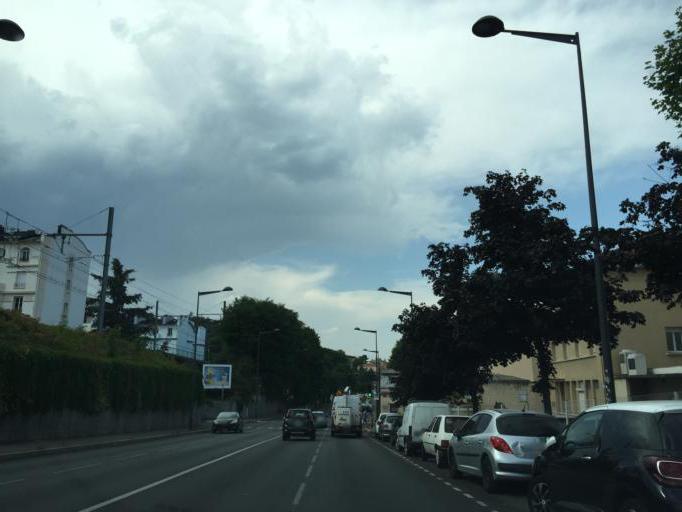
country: FR
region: Rhone-Alpes
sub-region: Departement de la Loire
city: Saint-Etienne
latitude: 45.4411
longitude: 4.3789
